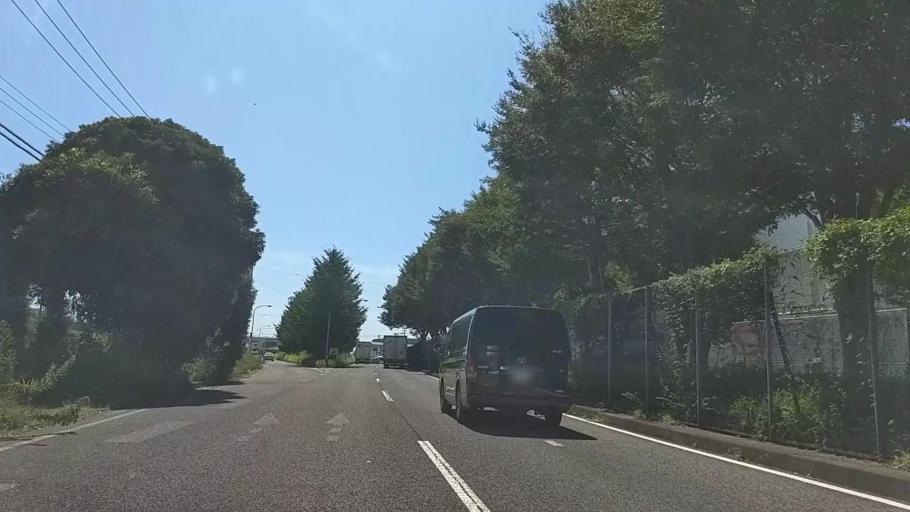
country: JP
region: Kanagawa
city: Zama
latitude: 35.5386
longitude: 139.3615
